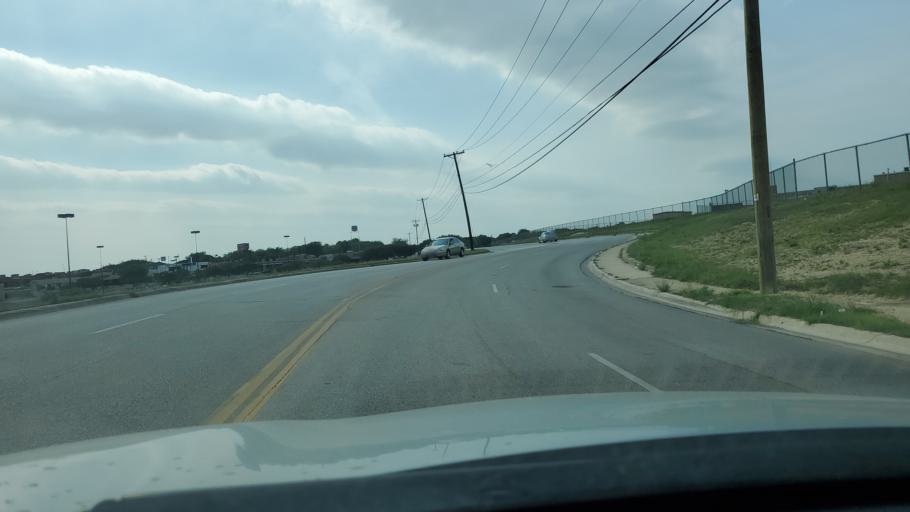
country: US
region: Texas
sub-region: Bell County
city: Killeen
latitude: 31.0947
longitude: -97.7169
